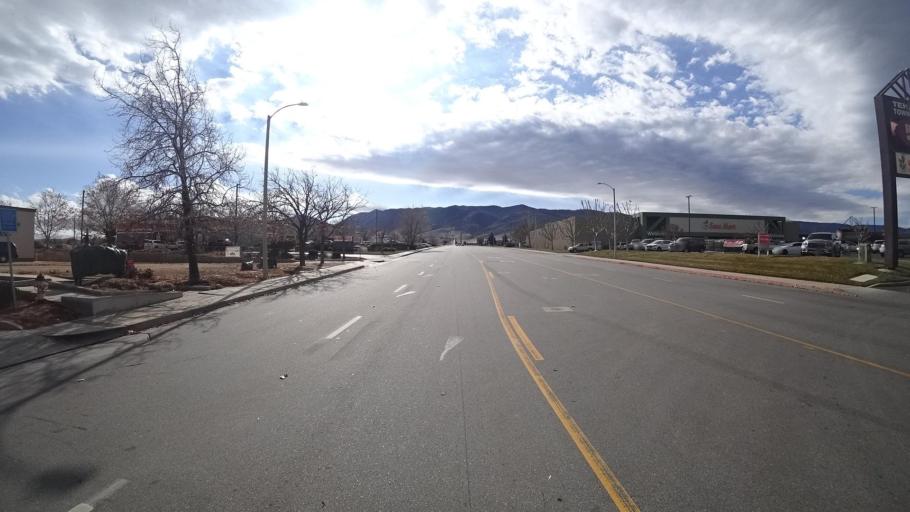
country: US
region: California
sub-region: Kern County
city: Tehachapi
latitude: 35.1235
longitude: -118.4678
